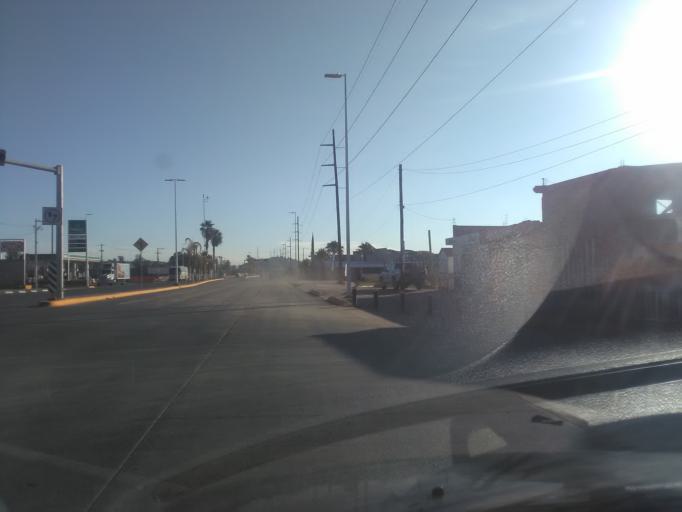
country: MX
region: Durango
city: Victoria de Durango
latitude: 23.9988
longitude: -104.7007
